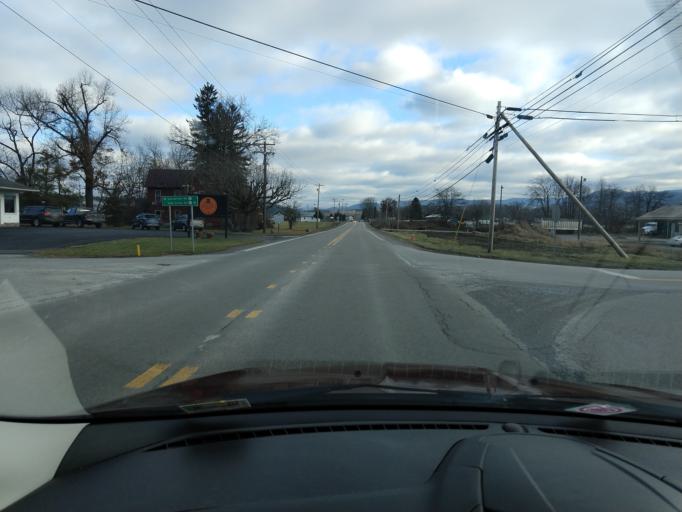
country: US
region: West Virginia
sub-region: Randolph County
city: Elkins
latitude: 38.7984
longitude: -79.8969
